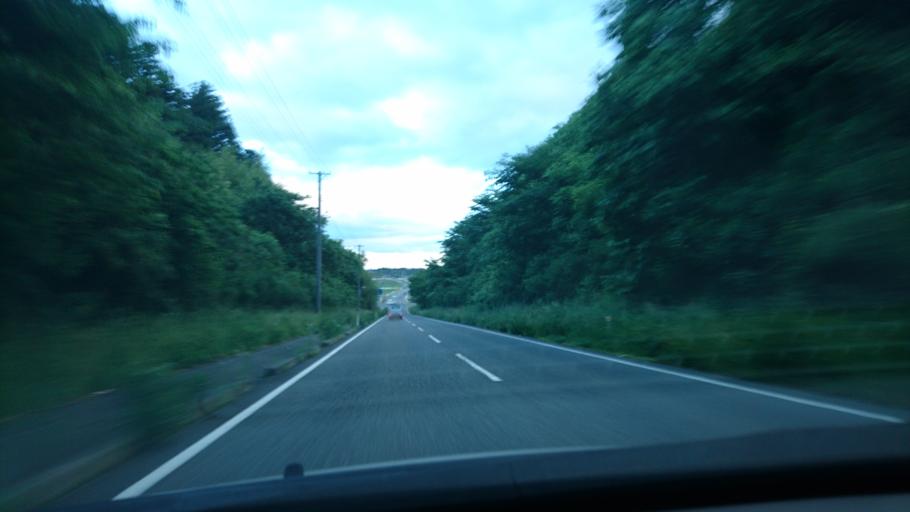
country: JP
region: Iwate
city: Ichinoseki
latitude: 38.7806
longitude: 141.0582
